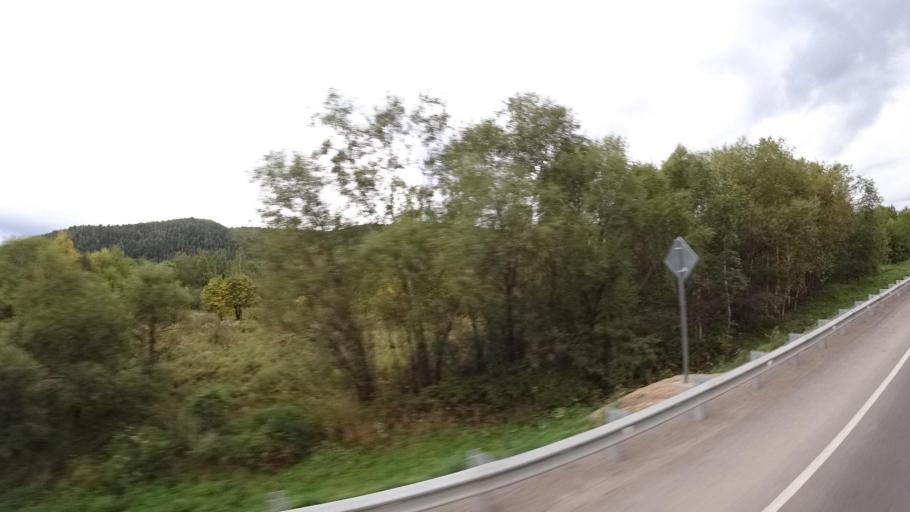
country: RU
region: Jewish Autonomous Oblast
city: Khingansk
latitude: 48.9866
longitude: 131.1367
